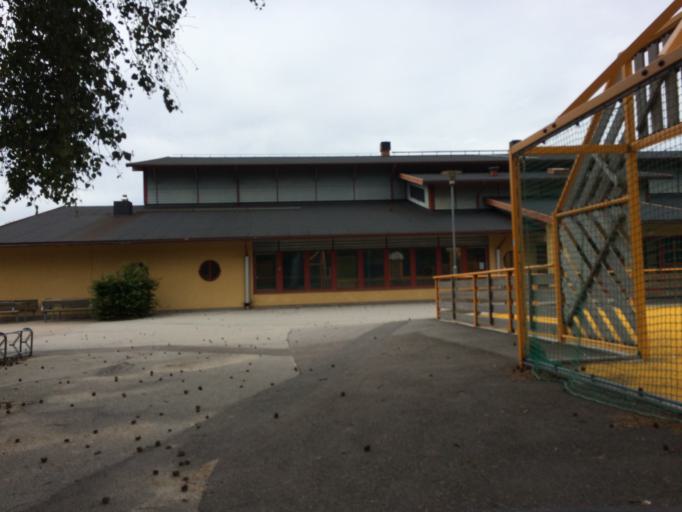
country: SE
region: Skane
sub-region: Vellinge Kommun
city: Ljunghusen
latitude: 55.4052
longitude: 12.9241
